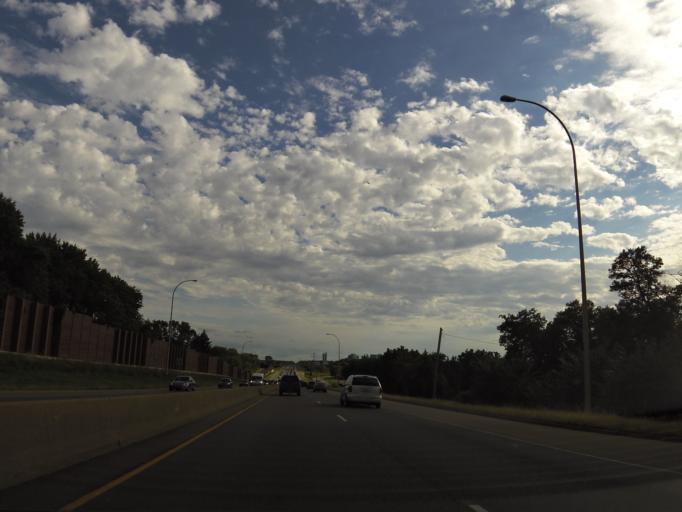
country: US
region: Minnesota
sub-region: Hennepin County
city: New Hope
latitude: 45.0004
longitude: -93.4010
